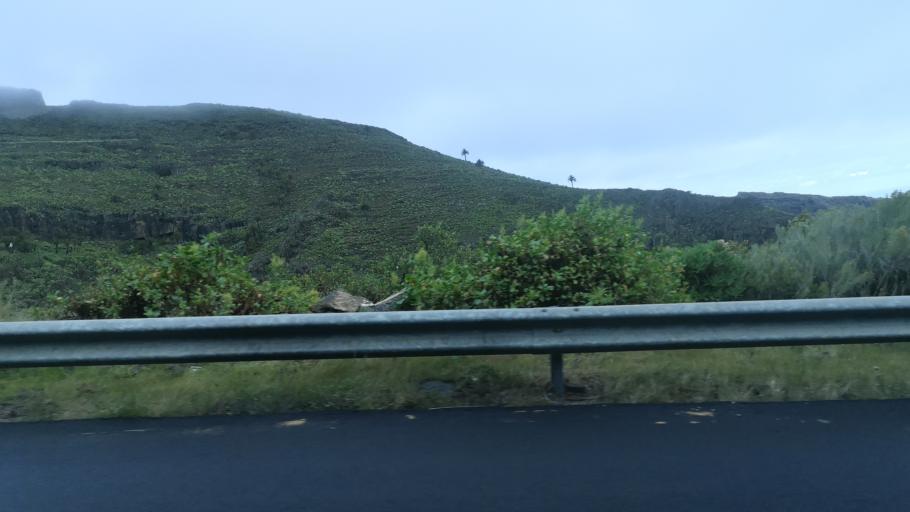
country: ES
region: Canary Islands
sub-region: Provincia de Santa Cruz de Tenerife
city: Alajero
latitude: 28.0700
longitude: -17.2069
